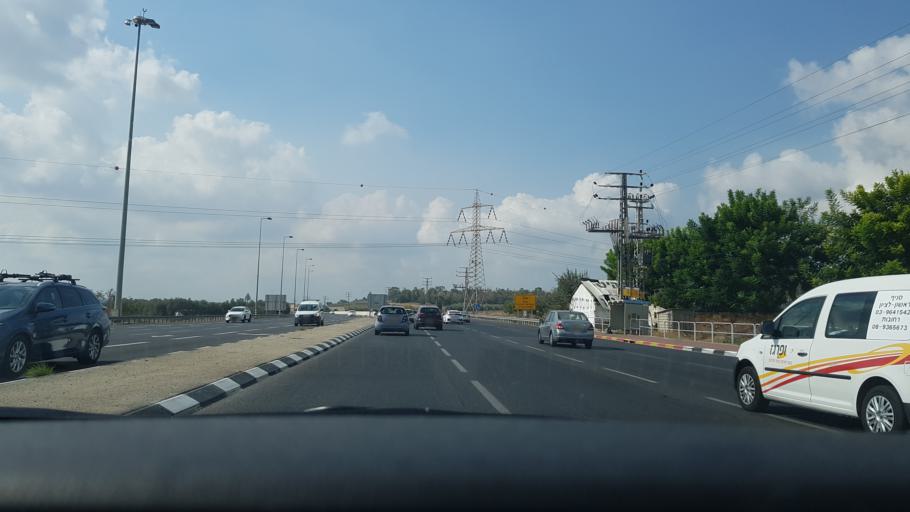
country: IL
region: Central District
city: Mazkeret Batya
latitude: 31.8605
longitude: 34.8078
